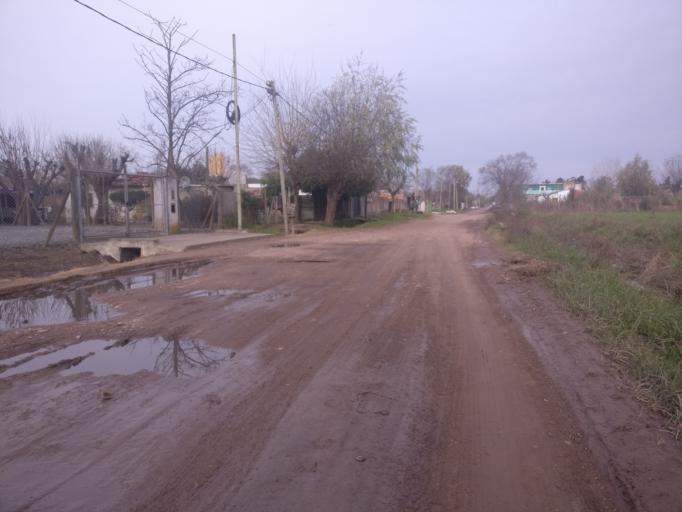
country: AR
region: Buenos Aires
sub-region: Partido de Ezeiza
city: Ezeiza
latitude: -34.9353
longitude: -58.6178
